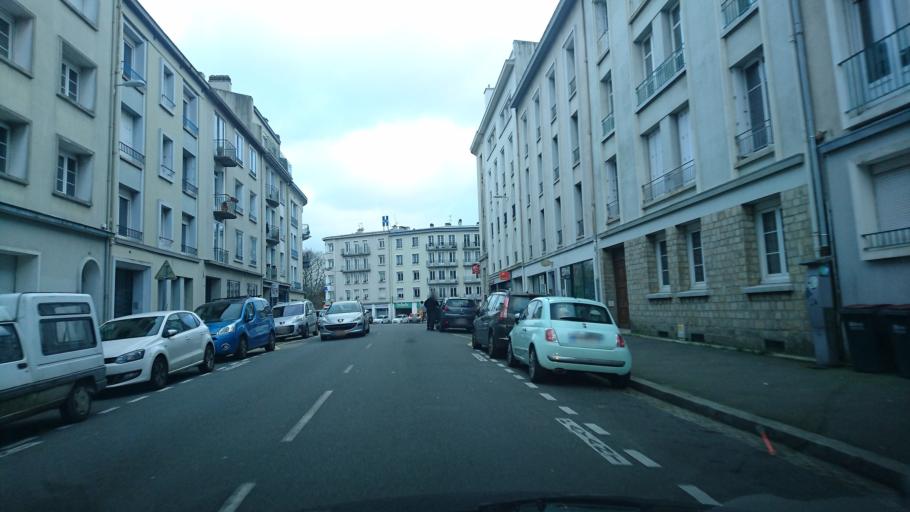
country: FR
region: Brittany
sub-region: Departement du Finistere
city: Brest
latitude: 48.3871
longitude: -4.4858
